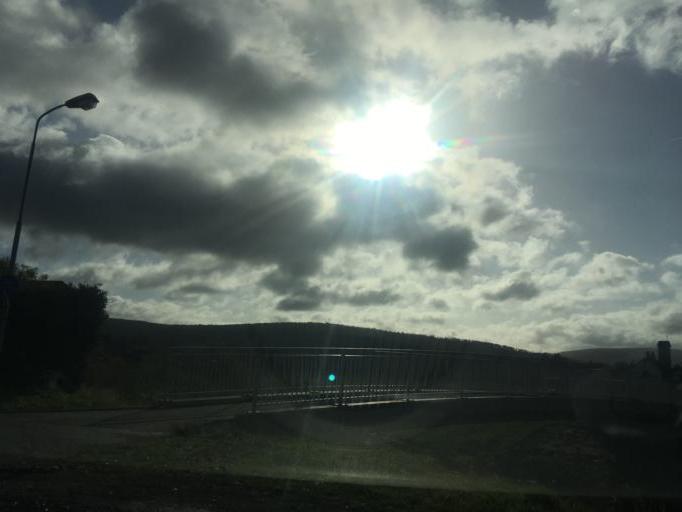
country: DE
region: Lower Saxony
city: Bodenfelde
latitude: 51.6320
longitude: 9.5589
